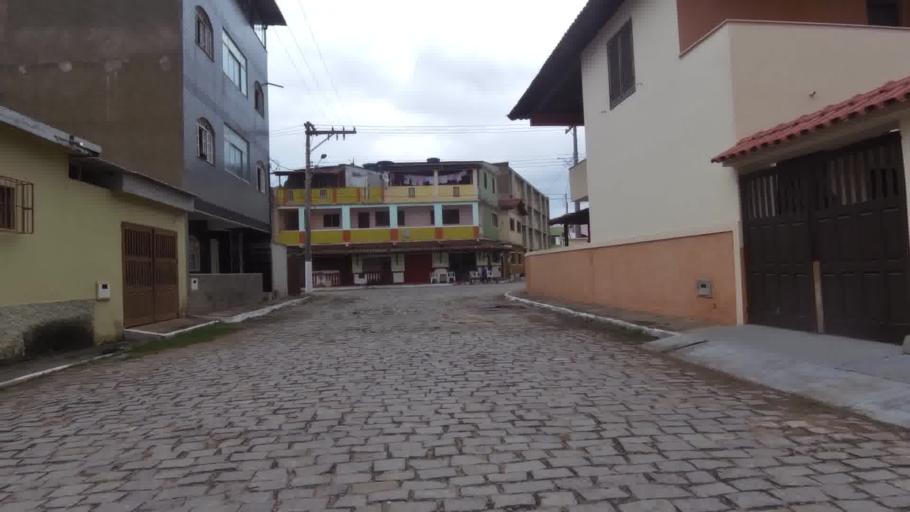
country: BR
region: Espirito Santo
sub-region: Marataizes
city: Marataizes
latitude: -21.0489
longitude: -40.8316
